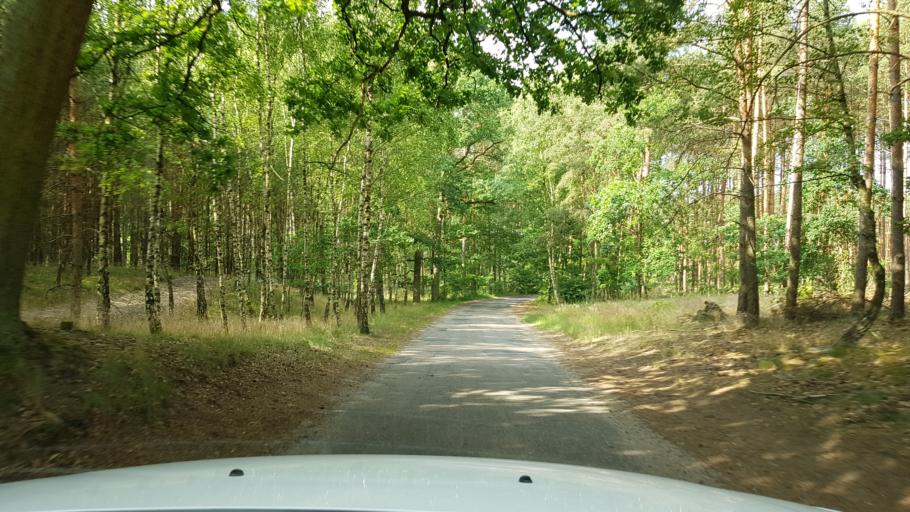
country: PL
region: West Pomeranian Voivodeship
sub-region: Powiat gryfinski
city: Gryfino
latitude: 53.2421
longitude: 14.5585
